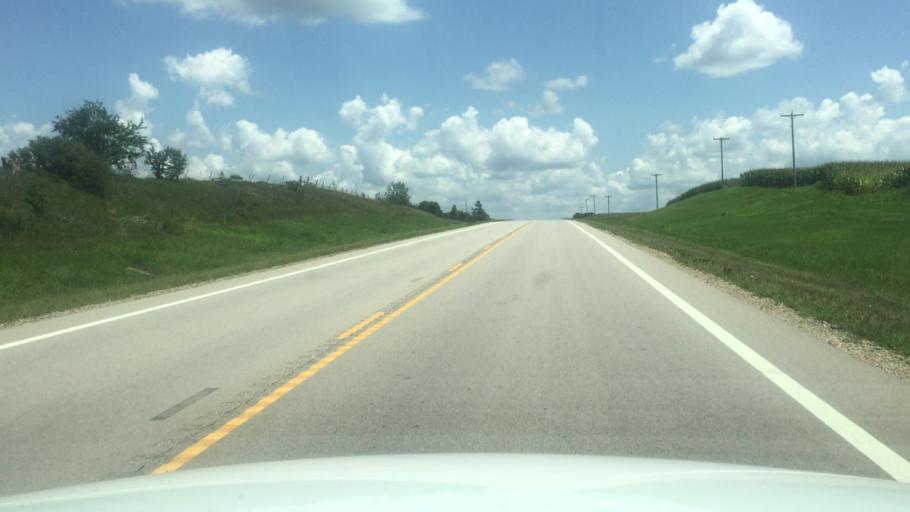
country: US
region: Kansas
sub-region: Brown County
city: Horton
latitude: 39.6672
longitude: -95.4703
